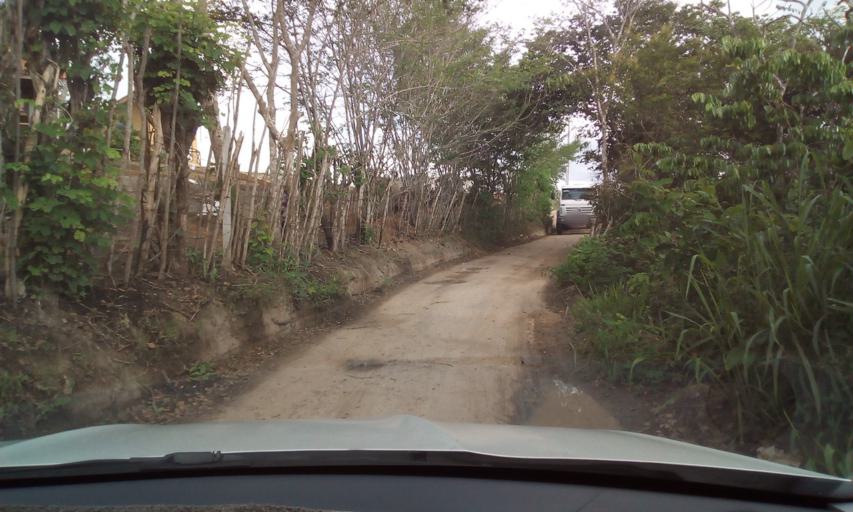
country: BR
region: Pernambuco
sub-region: Cha Grande
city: Cha Grande
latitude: -8.1975
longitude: -35.4938
